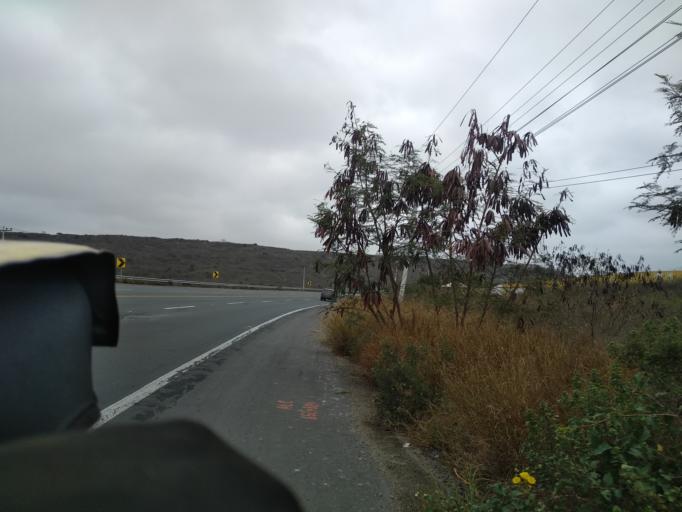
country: EC
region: Santa Elena
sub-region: Canton Santa Elena
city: Santa Elena
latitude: -2.2046
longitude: -80.8547
